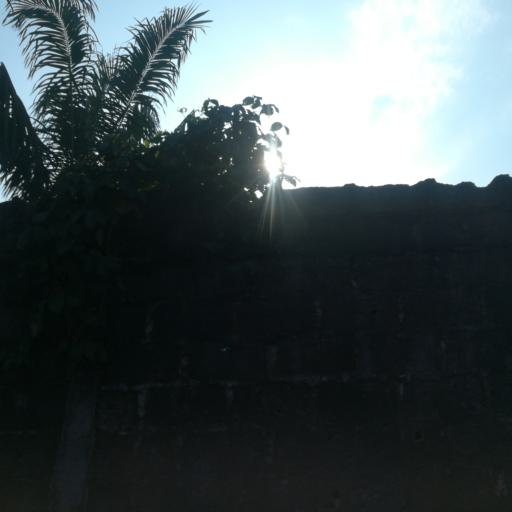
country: NG
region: Rivers
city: Port Harcourt
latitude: 4.8552
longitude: 6.9610
